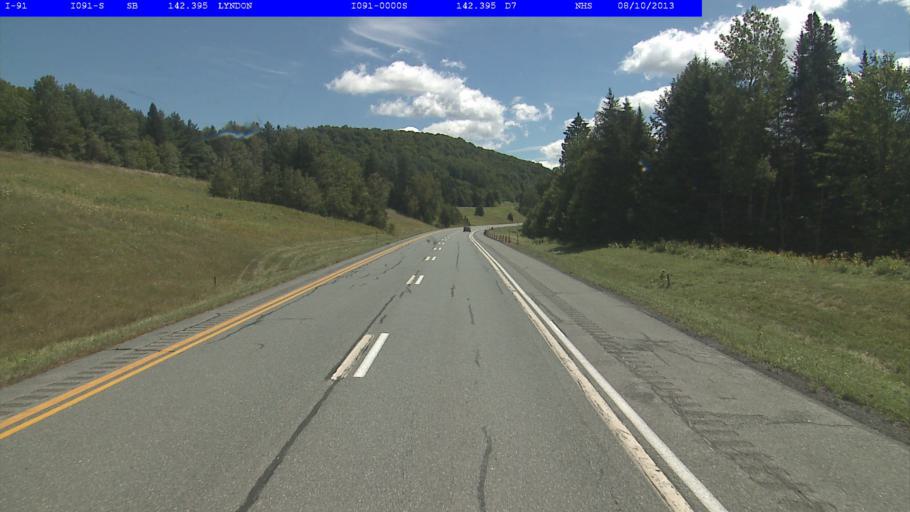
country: US
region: Vermont
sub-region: Caledonia County
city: Lyndonville
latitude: 44.5805
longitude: -72.0560
